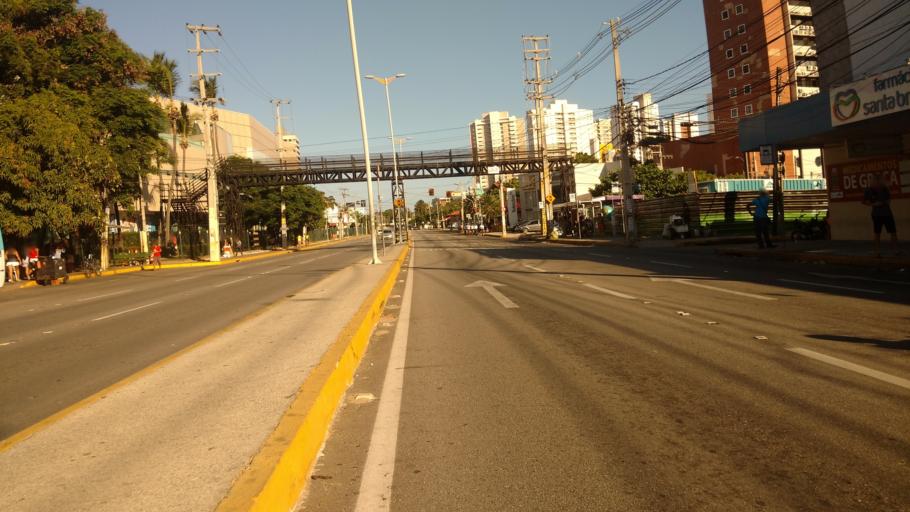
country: BR
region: Ceara
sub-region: Fortaleza
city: Fortaleza
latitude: -3.7575
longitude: -38.4894
